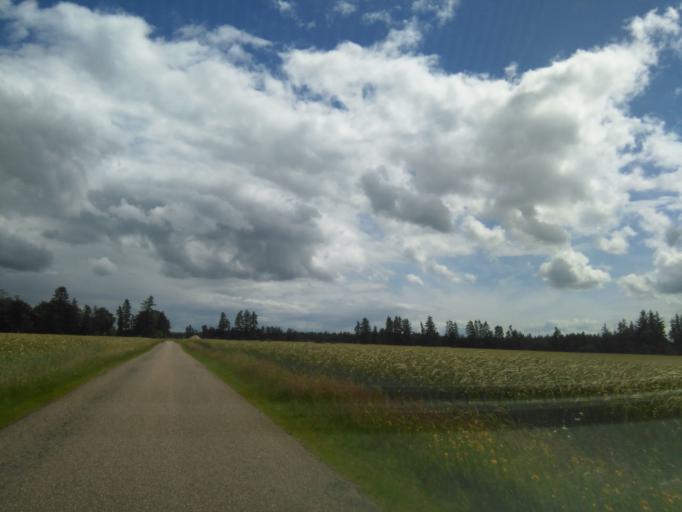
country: DK
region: Central Jutland
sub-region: Silkeborg Kommune
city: Virklund
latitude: 56.0381
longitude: 9.3925
